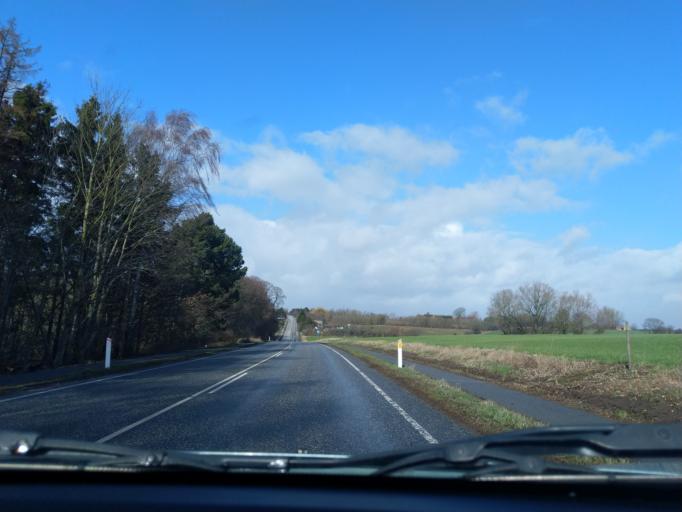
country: DK
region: Zealand
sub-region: Naestved Kommune
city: Naestved
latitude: 55.3009
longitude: 11.6915
